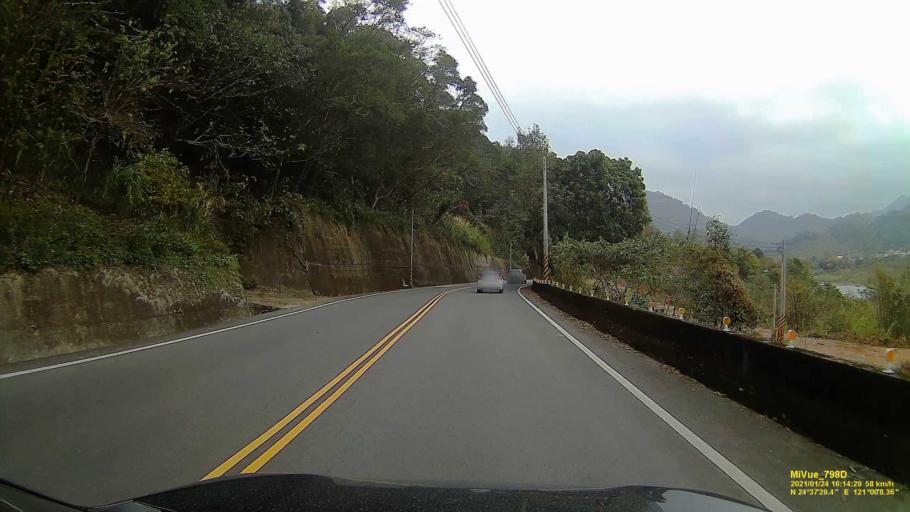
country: TW
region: Taiwan
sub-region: Hsinchu
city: Hsinchu
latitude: 24.6252
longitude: 121.0025
